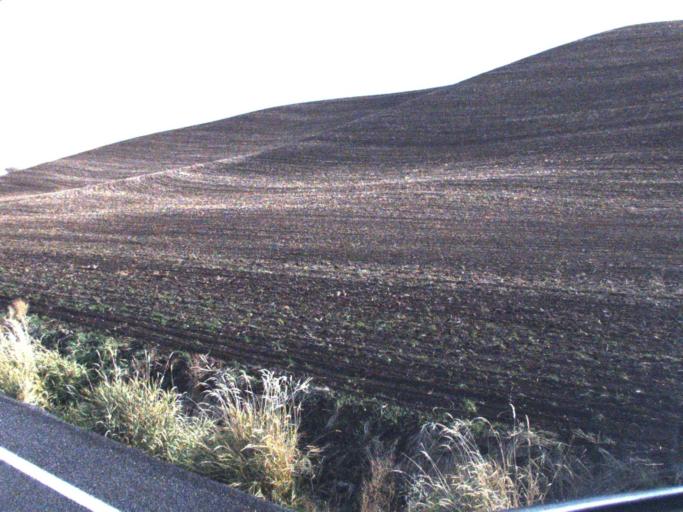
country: US
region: Washington
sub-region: Whitman County
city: Colfax
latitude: 46.7478
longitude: -117.4606
